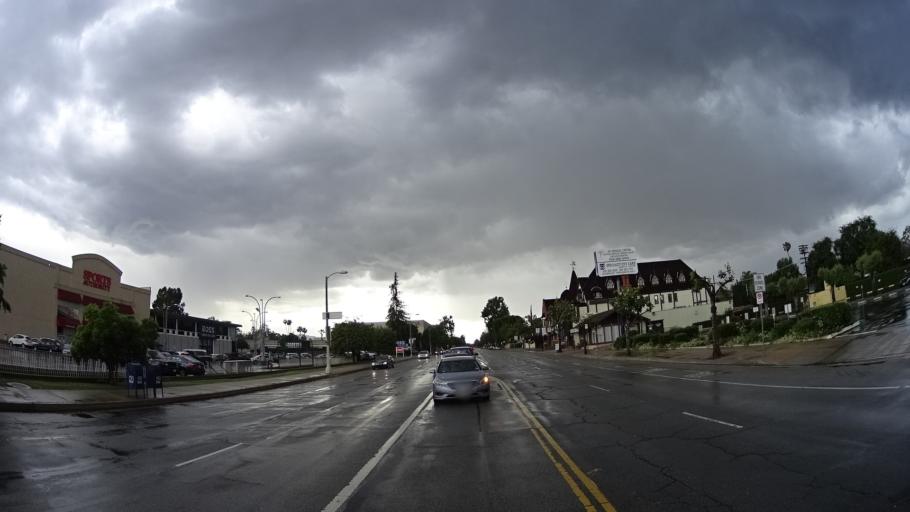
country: US
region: California
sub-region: Los Angeles County
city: Sherman Oaks
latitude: 34.1576
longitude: -118.4319
